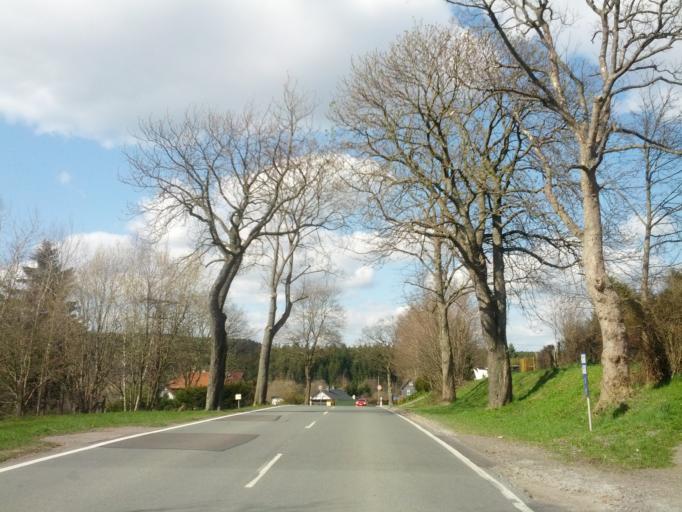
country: DE
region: Thuringia
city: Tambach-Dietharz
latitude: 50.8035
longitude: 10.6206
